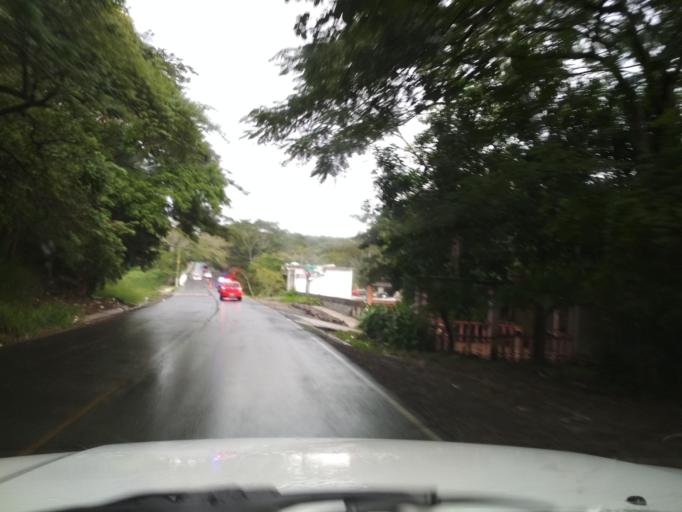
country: MX
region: Veracruz
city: Santiago Tuxtla
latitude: 18.4464
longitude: -95.3176
